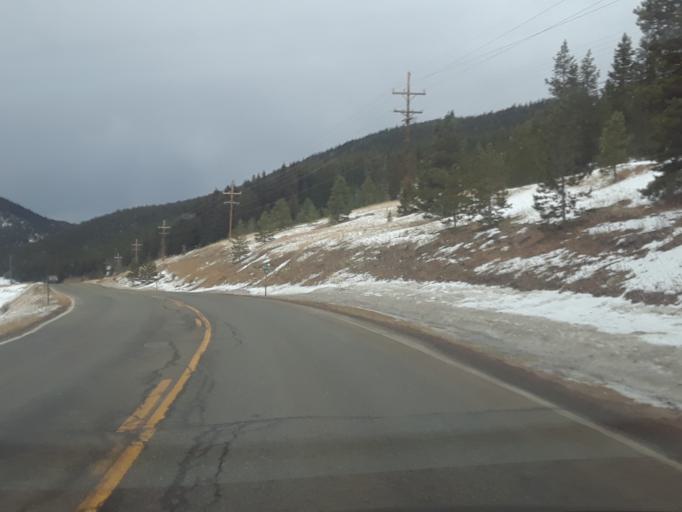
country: US
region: Colorado
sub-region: Gilpin County
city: Central City
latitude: 39.8341
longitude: -105.4314
